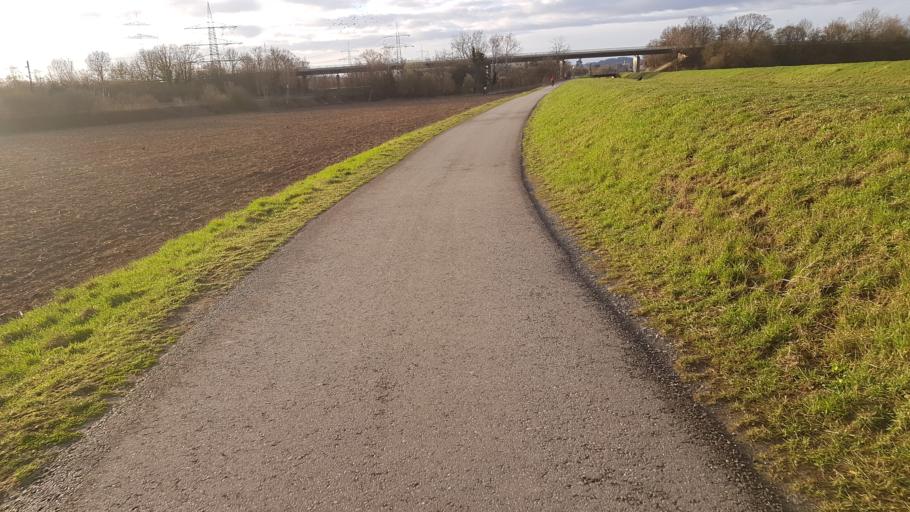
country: DE
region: Baden-Wuerttemberg
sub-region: Karlsruhe Region
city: Walldorf
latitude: 49.3127
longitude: 8.6660
